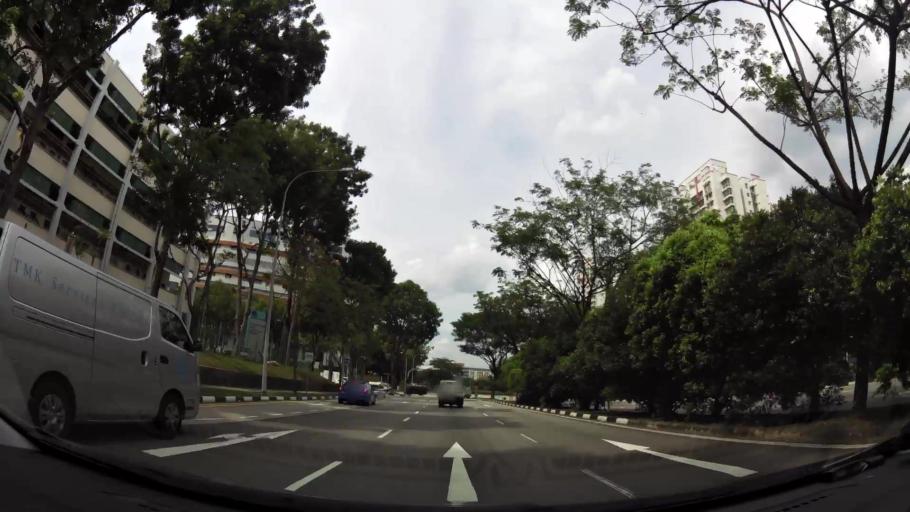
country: MY
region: Johor
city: Johor Bahru
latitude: 1.4541
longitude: 103.8126
